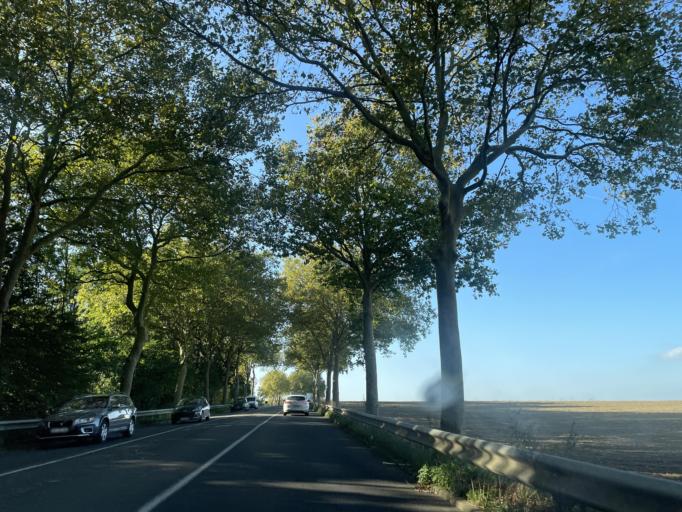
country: FR
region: Ile-de-France
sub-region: Departement de Seine-et-Marne
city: La Chapelle-sur-Crecy
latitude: 48.8463
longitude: 2.9449
